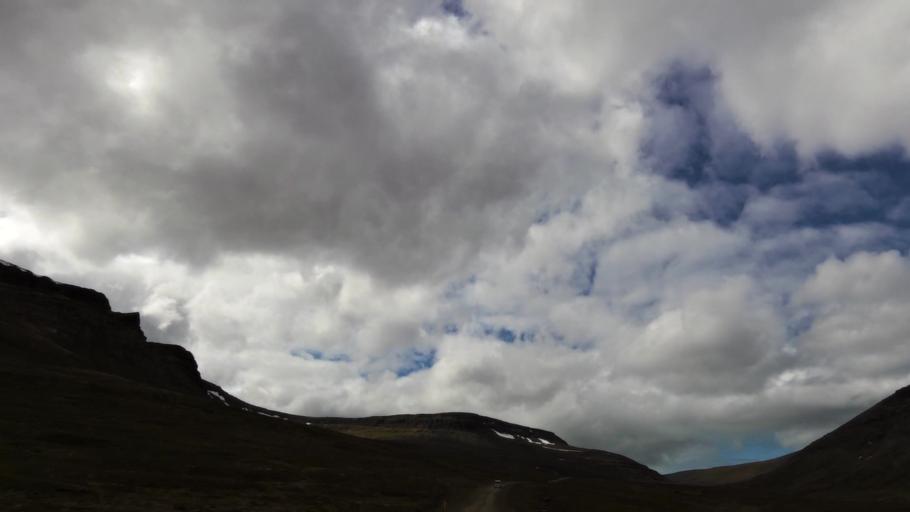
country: IS
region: Westfjords
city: Isafjoerdur
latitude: 66.1616
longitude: -23.3068
